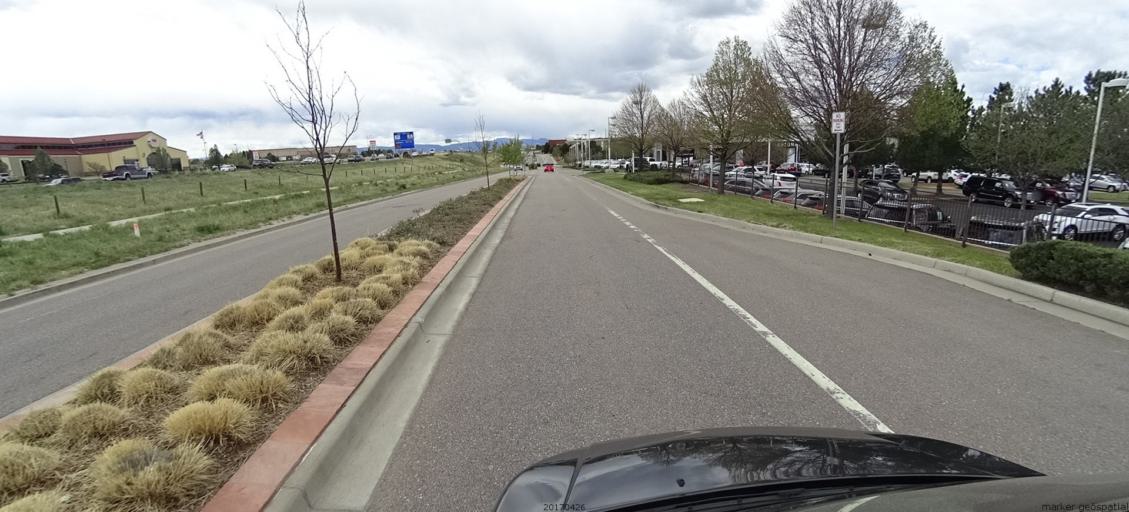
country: US
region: Colorado
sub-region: Douglas County
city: Acres Green
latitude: 39.5648
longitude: -104.8940
